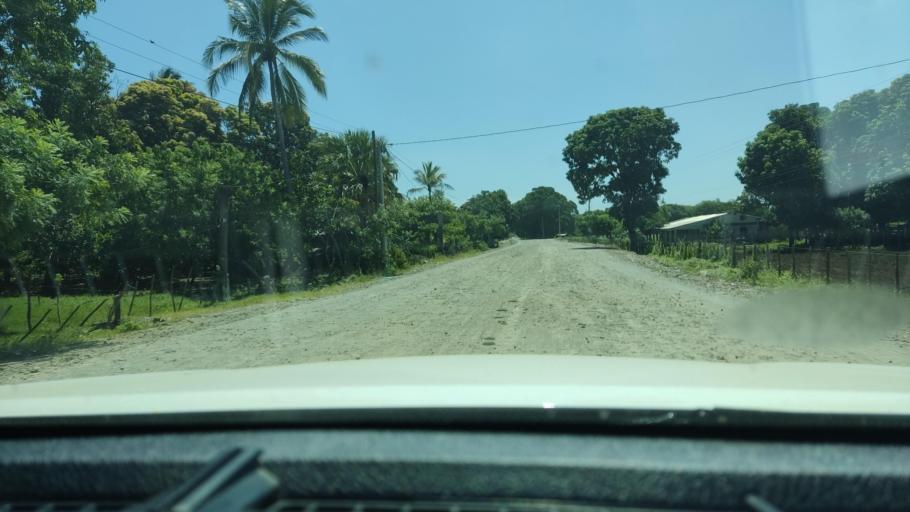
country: SV
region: Ahuachapan
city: San Francisco Menendez
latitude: 13.7548
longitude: -90.1313
